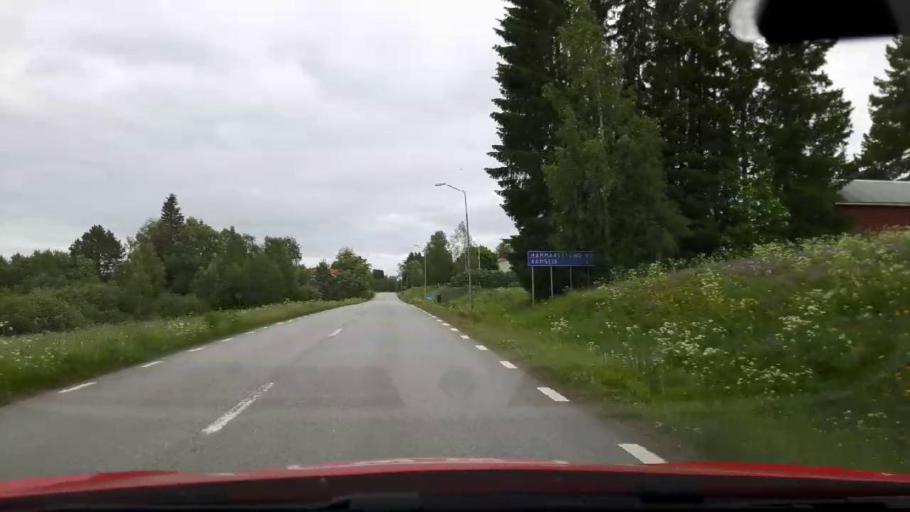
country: SE
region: Jaemtland
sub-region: Stroemsunds Kommun
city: Stroemsund
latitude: 63.5780
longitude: 15.3685
